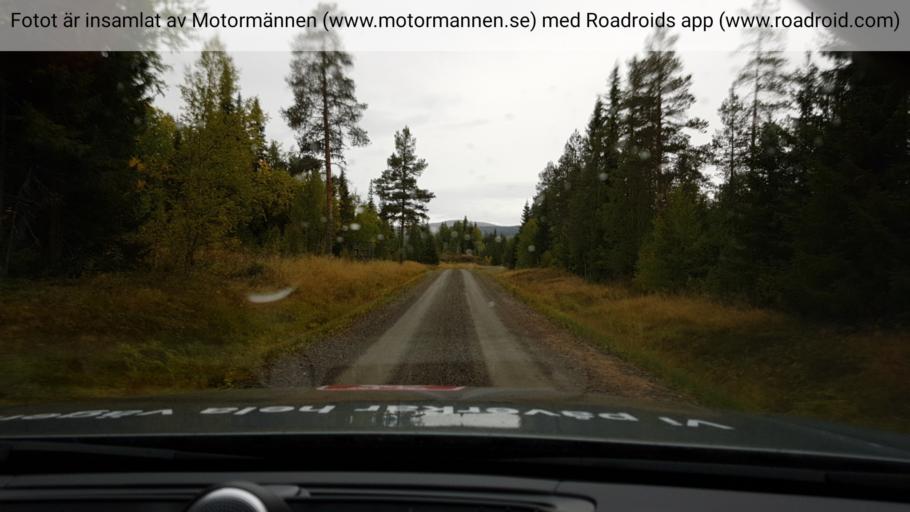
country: NO
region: Nord-Trondelag
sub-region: Lierne
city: Sandvika
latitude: 64.4320
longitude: 14.4435
